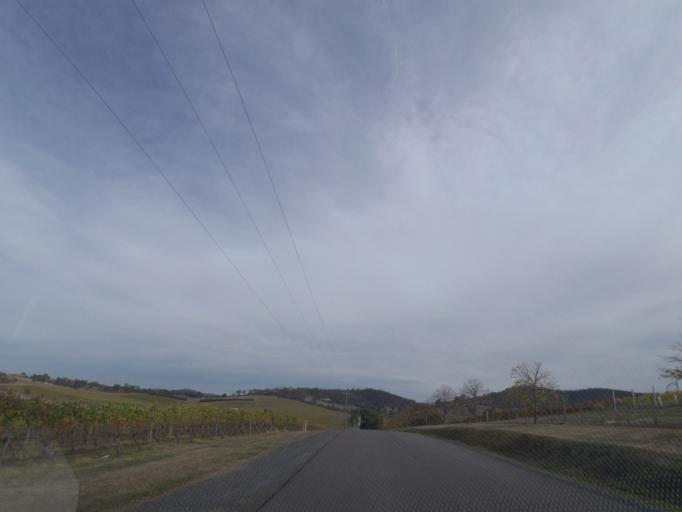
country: AU
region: Victoria
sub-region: Yarra Ranges
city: Yarra Glen
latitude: -37.6011
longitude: 145.4144
